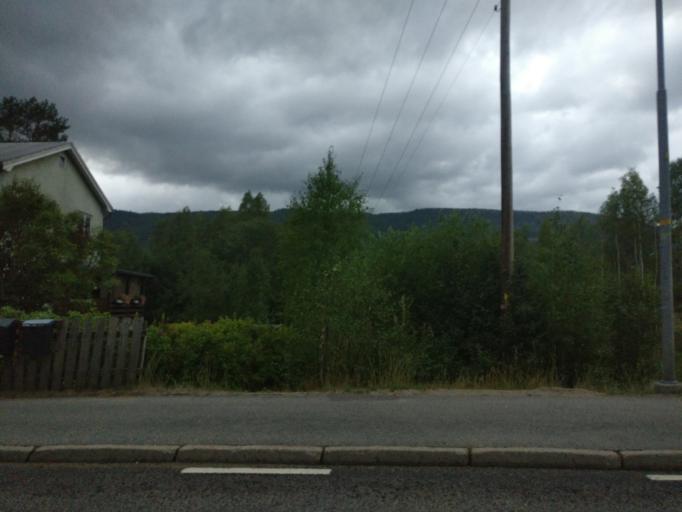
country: SE
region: Vaermland
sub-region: Torsby Kommun
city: Torsby
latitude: 60.7238
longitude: 12.8781
